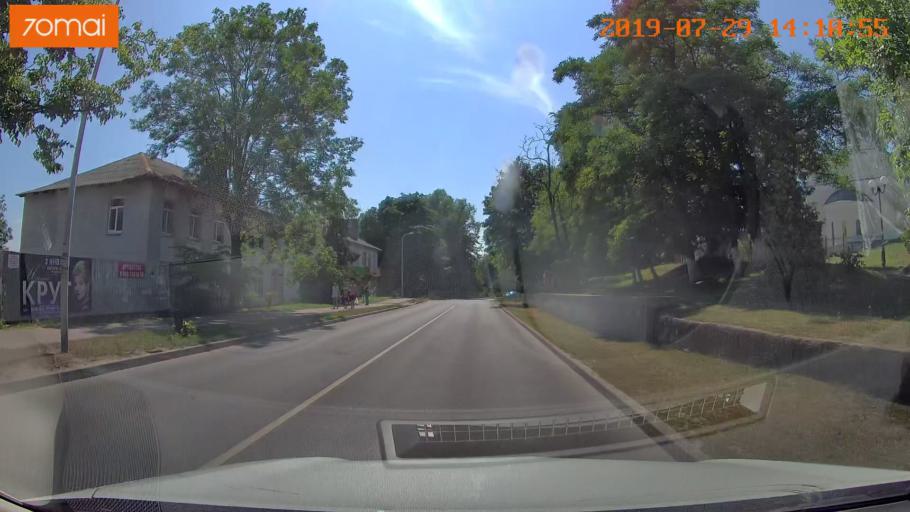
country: RU
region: Kaliningrad
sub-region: Gorod Kaliningrad
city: Baltiysk
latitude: 54.6535
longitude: 19.9110
